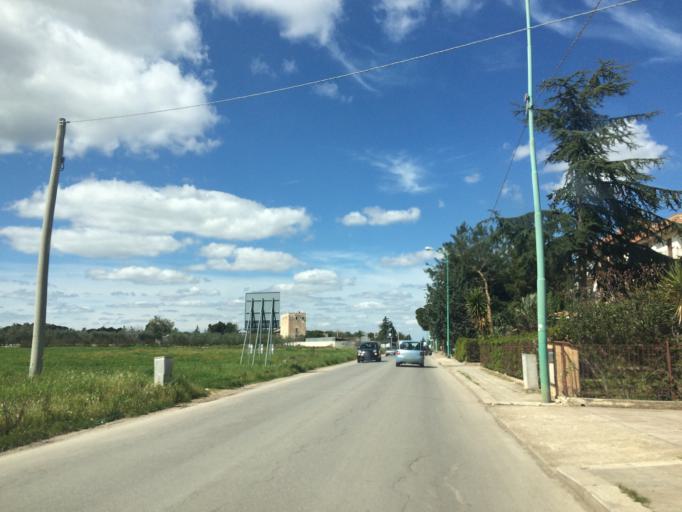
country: IT
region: Apulia
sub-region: Provincia di Bari
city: Terlizzi
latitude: 41.1270
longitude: 16.5380
